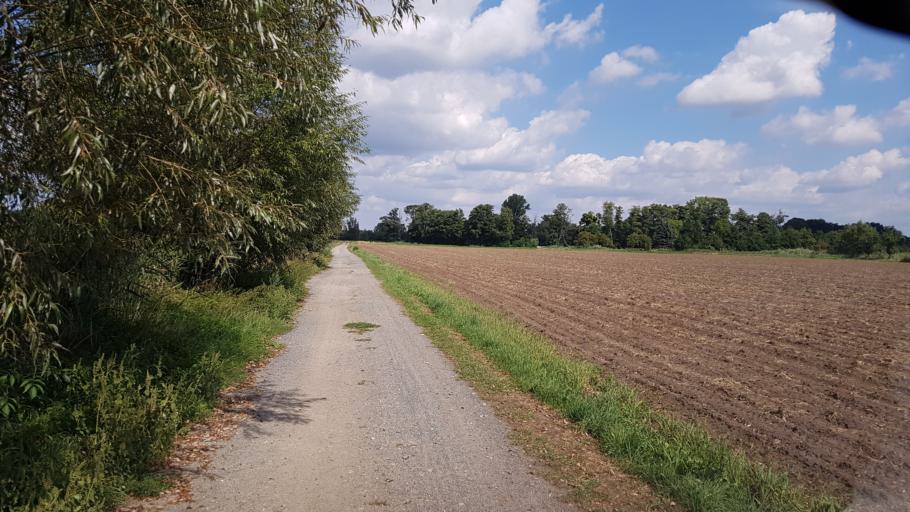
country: DE
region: Brandenburg
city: Lubbenau
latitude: 51.8677
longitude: 13.9280
